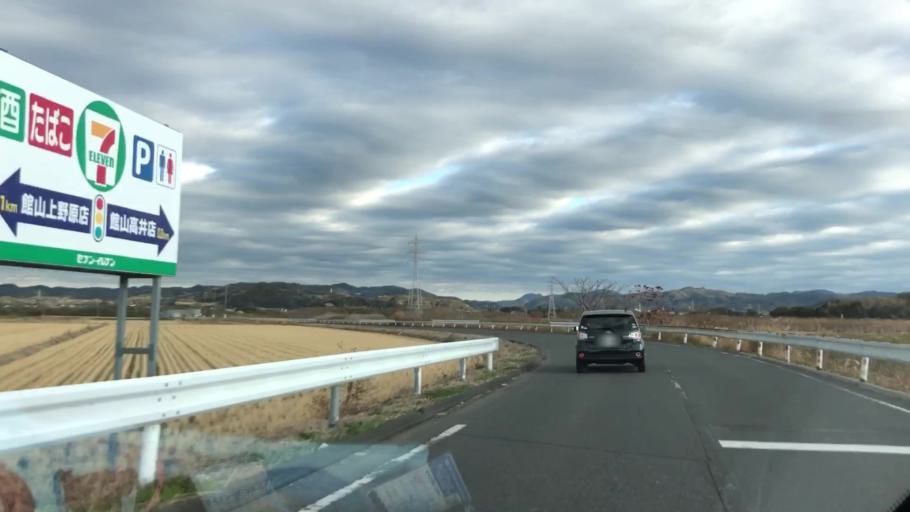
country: JP
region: Chiba
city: Tateyama
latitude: 35.0007
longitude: 139.8846
